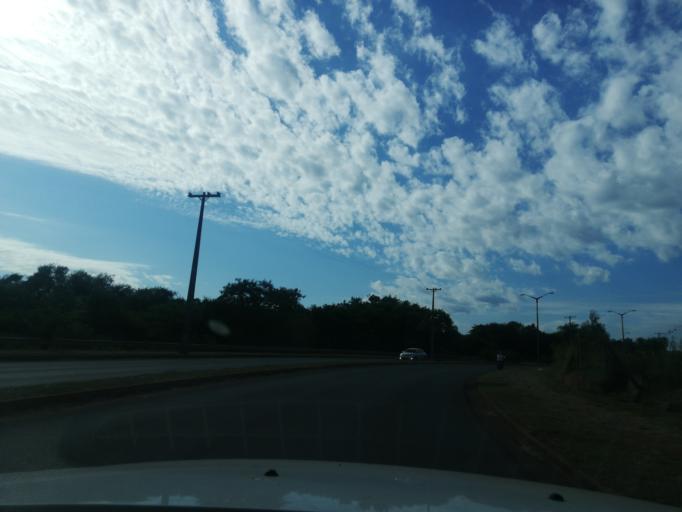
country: PY
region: Itapua
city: Encarnacion
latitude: -27.3472
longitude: -55.8493
